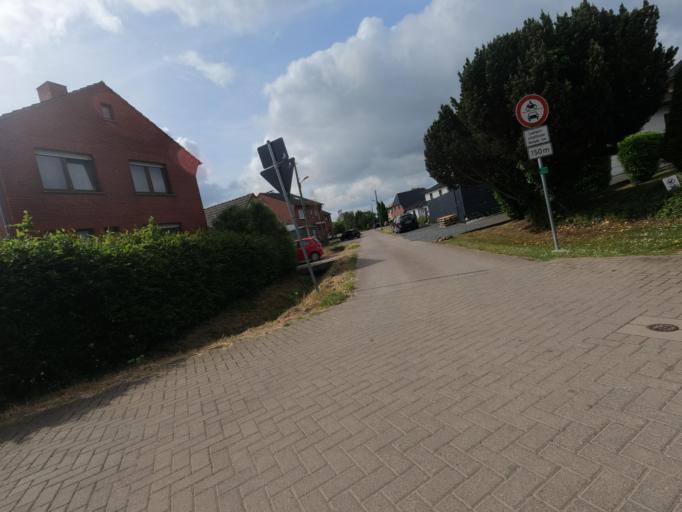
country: DE
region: North Rhine-Westphalia
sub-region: Regierungsbezirk Koln
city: Heinsberg
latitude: 51.0900
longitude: 6.1172
